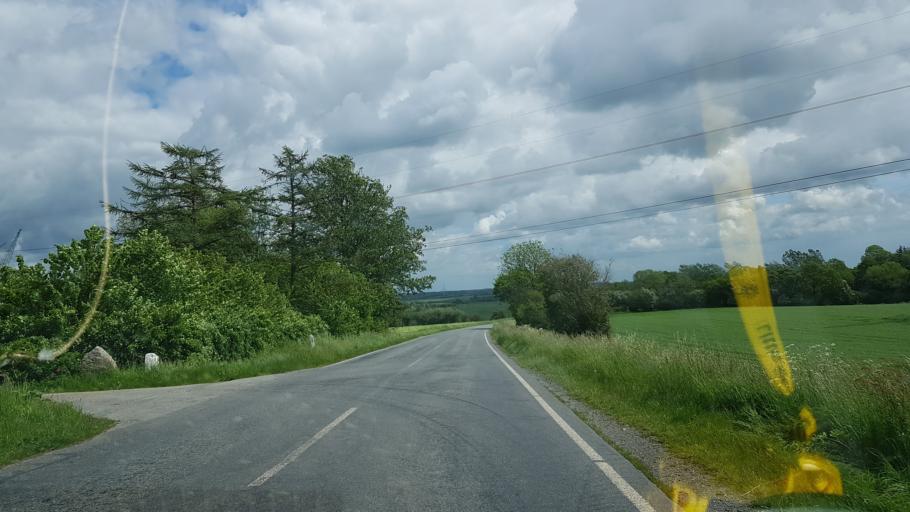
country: DK
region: South Denmark
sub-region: Kolding Kommune
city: Christiansfeld
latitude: 55.3325
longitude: 9.4294
